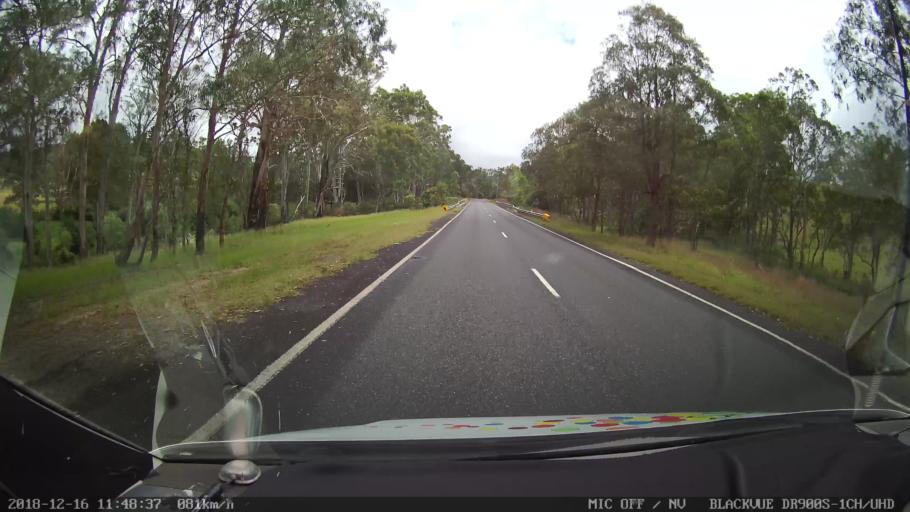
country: AU
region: New South Wales
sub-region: Tenterfield Municipality
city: Carrolls Creek
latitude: -28.9207
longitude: 152.2490
